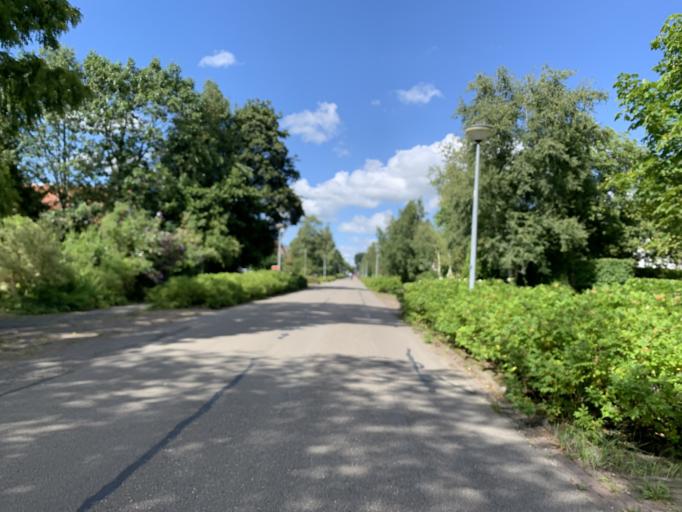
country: NL
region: Groningen
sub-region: Gemeente Groningen
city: Groningen
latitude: 53.1848
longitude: 6.5504
